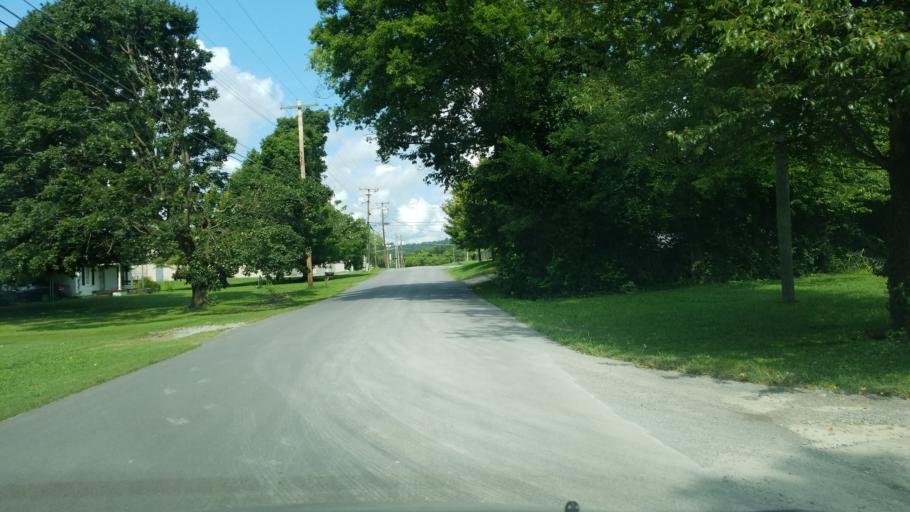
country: US
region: Tennessee
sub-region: Hamilton County
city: East Chattanooga
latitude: 35.0722
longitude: -85.2656
